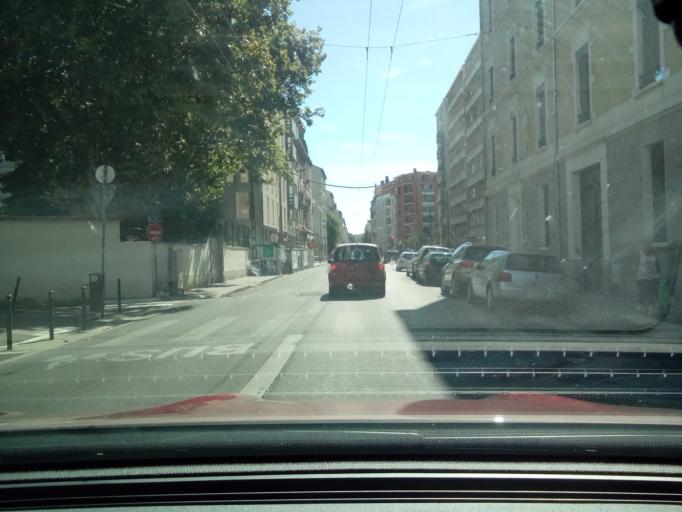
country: FR
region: Rhone-Alpes
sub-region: Departement du Rhone
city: Villeurbanne
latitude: 45.7623
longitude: 4.8792
